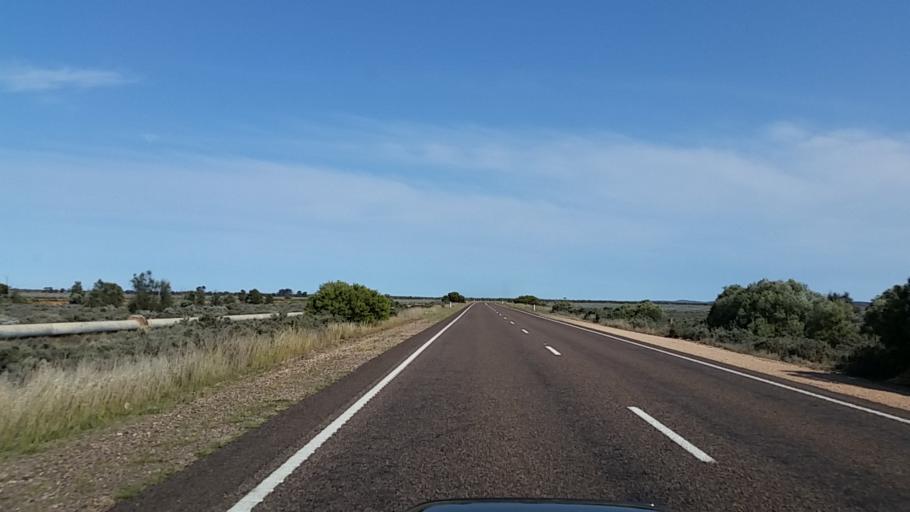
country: AU
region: South Australia
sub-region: Whyalla
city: Whyalla
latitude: -32.8653
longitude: 137.5546
